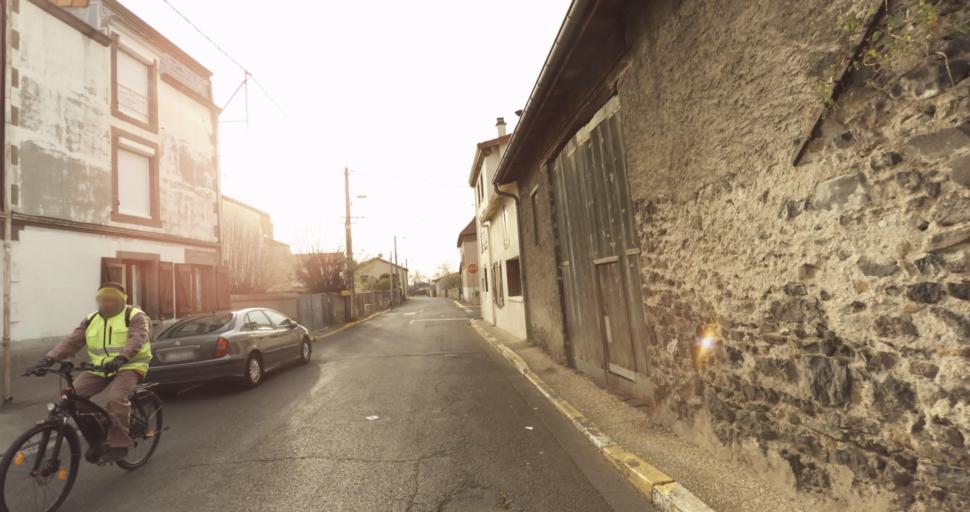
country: FR
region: Auvergne
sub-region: Departement du Puy-de-Dome
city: Cebazat
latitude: 45.8330
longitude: 3.1014
